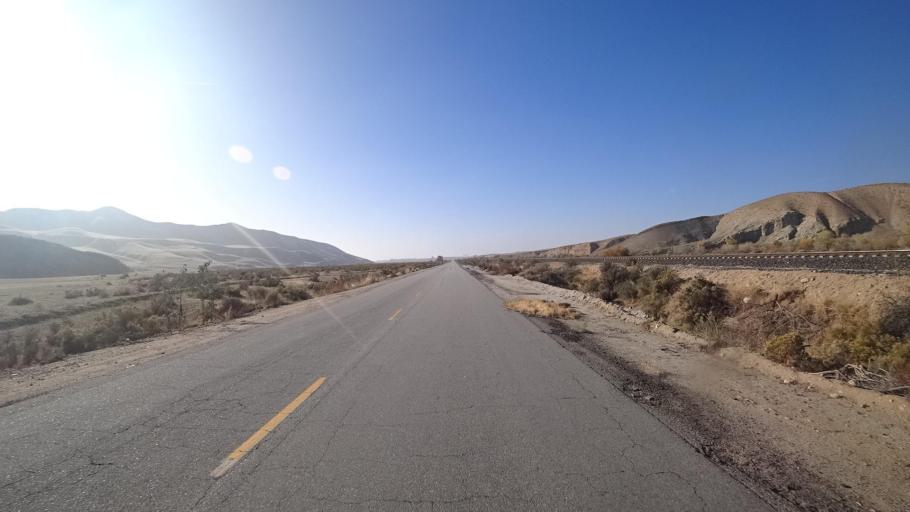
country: US
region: California
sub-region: Kern County
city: Arvin
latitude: 35.3237
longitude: -118.7206
